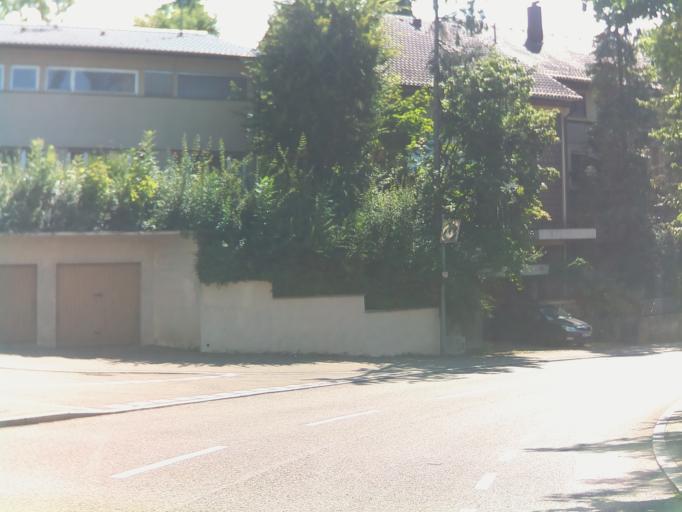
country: DE
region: Baden-Wuerttemberg
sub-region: Regierungsbezirk Stuttgart
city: Leonberg
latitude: 48.8032
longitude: 9.0199
